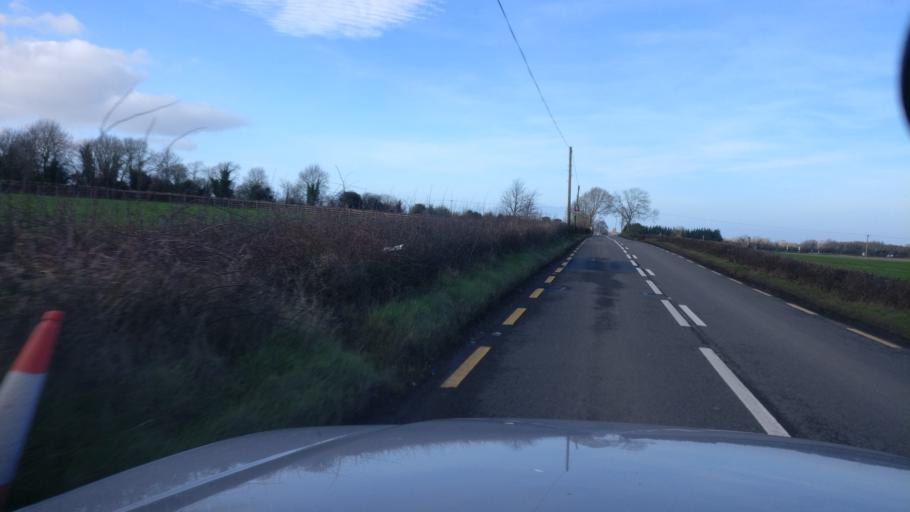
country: IE
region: Leinster
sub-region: Laois
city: Mountmellick
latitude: 53.0965
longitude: -7.3375
